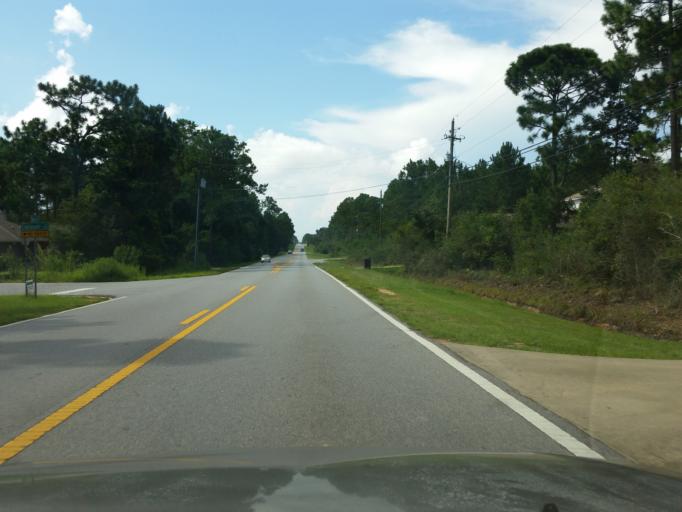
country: US
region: Florida
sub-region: Escambia County
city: Myrtle Grove
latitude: 30.3557
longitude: -87.4029
